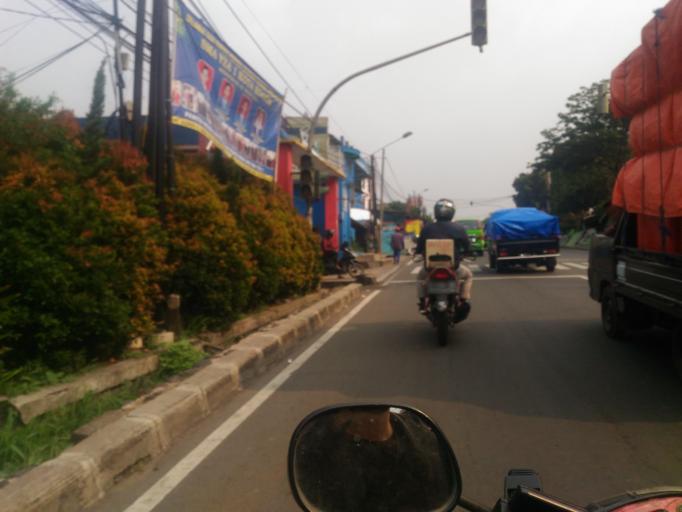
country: ID
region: West Java
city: Caringin
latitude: -6.6515
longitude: 106.8452
